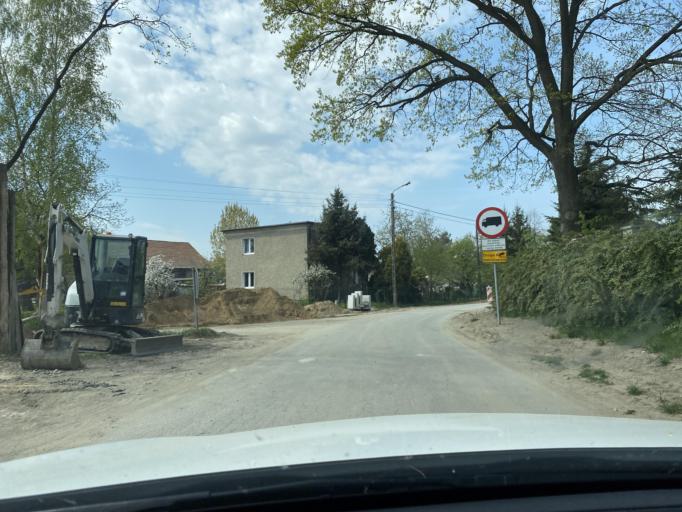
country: PL
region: Lower Silesian Voivodeship
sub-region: Powiat wroclawski
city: Mirkow
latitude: 51.1587
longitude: 17.1732
